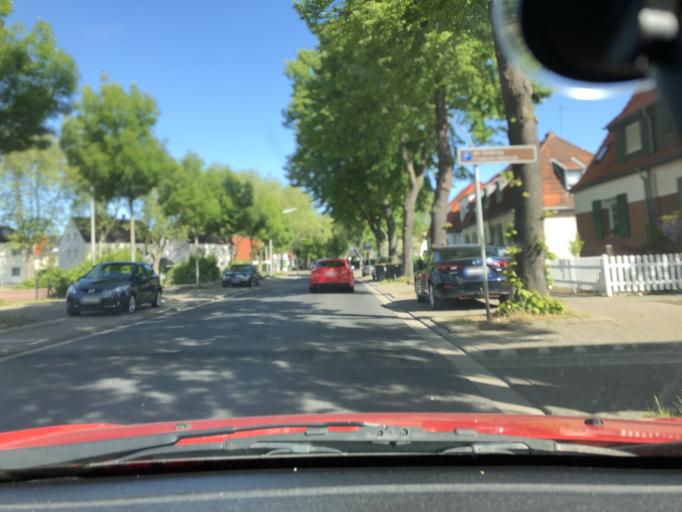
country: DE
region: North Rhine-Westphalia
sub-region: Regierungsbezirk Dusseldorf
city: Kamp-Lintfort
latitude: 51.4938
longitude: 6.5568
